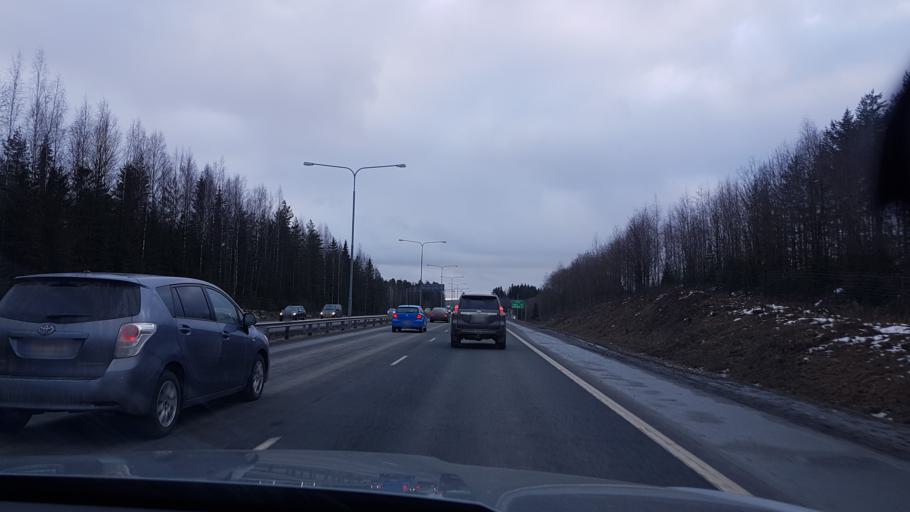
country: FI
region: Pirkanmaa
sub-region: Tampere
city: Tampere
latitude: 61.4412
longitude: 23.7608
